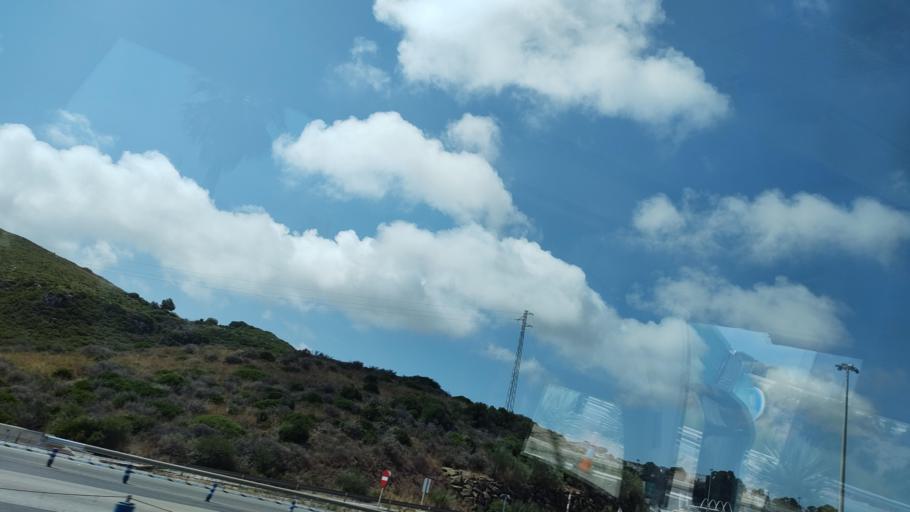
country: ES
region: Andalusia
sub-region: Provincia de Malaga
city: Manilva
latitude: 36.3766
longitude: -5.2644
